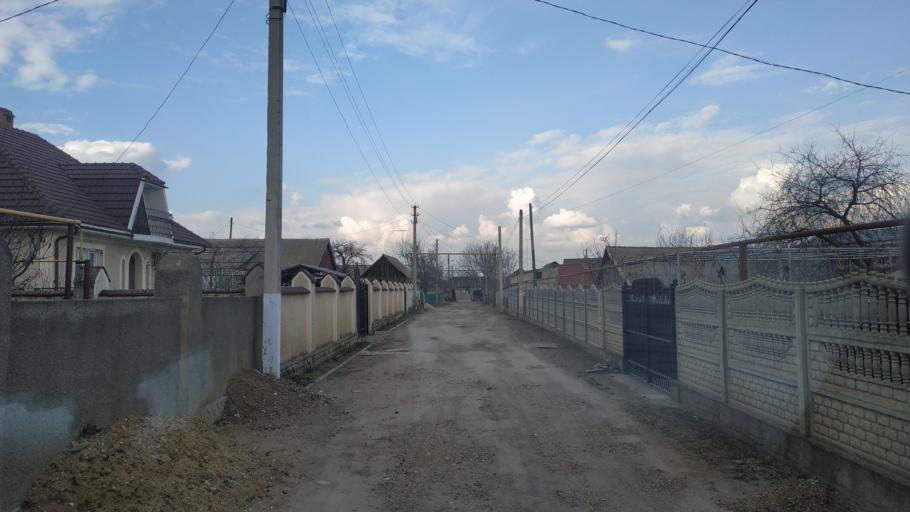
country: MD
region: Anenii Noi
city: Varnita
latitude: 46.8600
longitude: 29.4754
